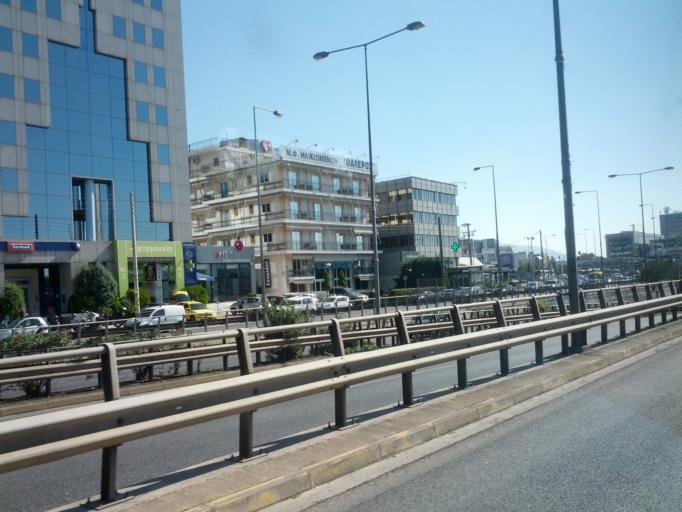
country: GR
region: Attica
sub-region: Nomarchia Athinas
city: Marousi
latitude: 38.0440
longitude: 23.8048
